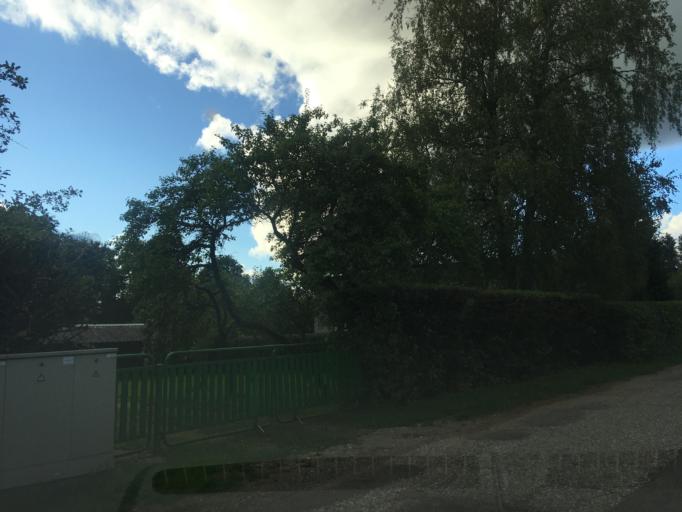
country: EE
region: Raplamaa
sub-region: Maerjamaa vald
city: Marjamaa
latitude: 58.9036
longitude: 24.4377
